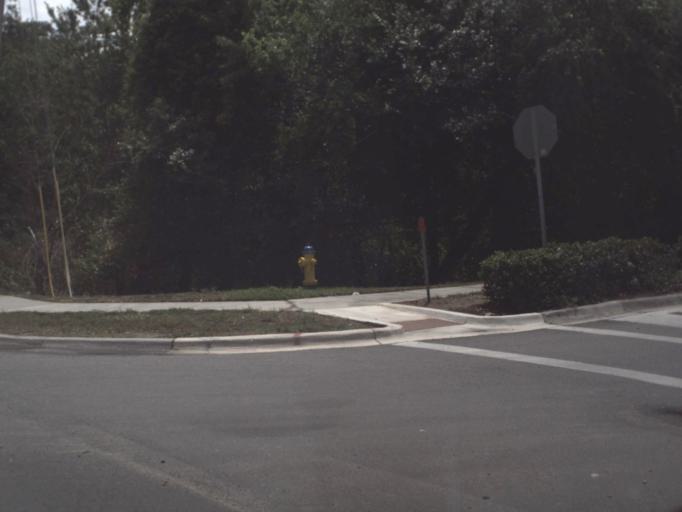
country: US
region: Florida
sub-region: Lake County
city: Groveland
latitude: 28.5580
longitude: -81.8504
